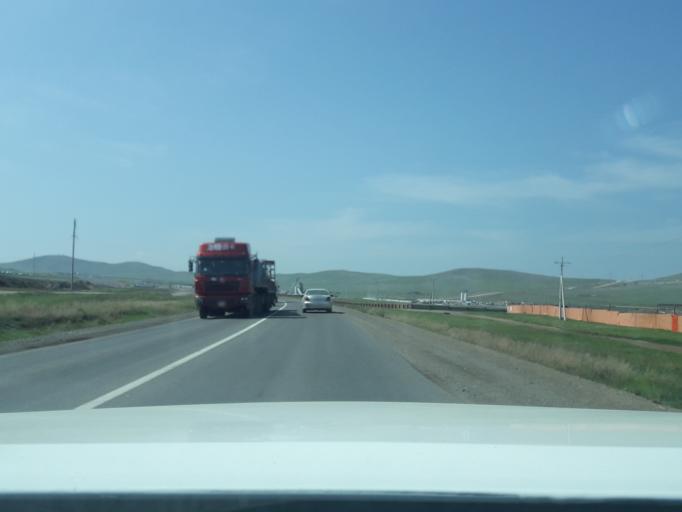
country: MN
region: Ulaanbaatar
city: Ulaanbaatar
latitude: 47.8245
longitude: 106.7660
